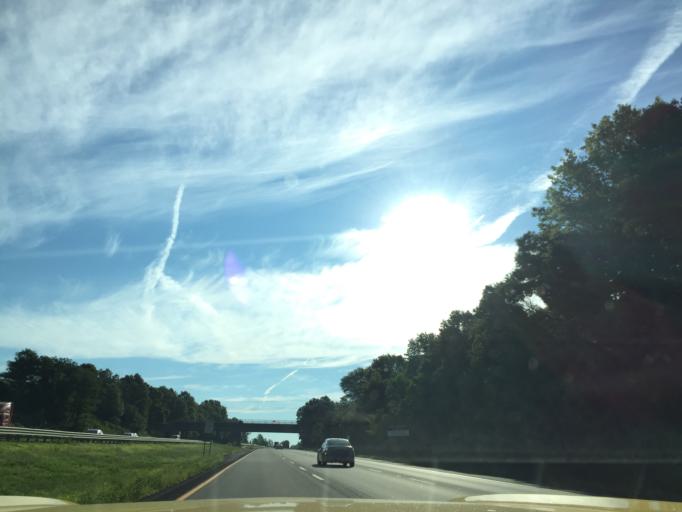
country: US
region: New Jersey
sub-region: Hunterdon County
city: Annandale
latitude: 40.6440
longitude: -74.8636
